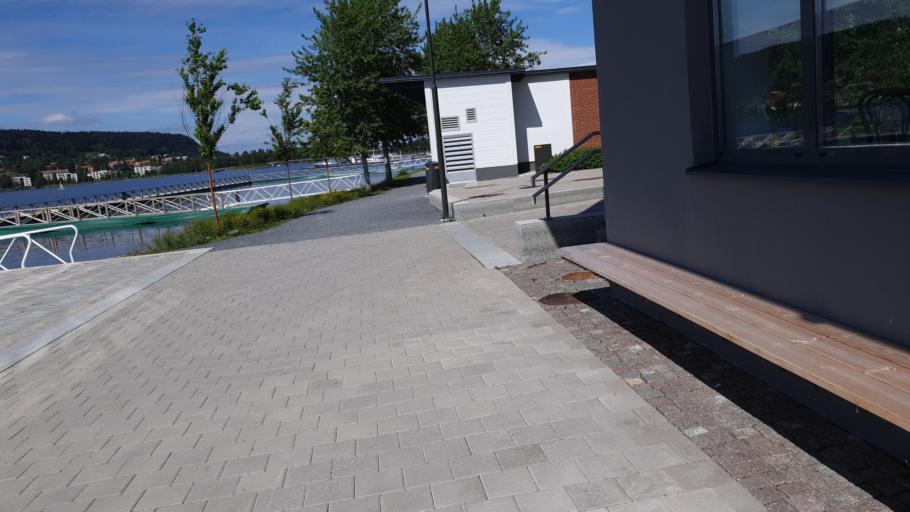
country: SE
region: Jaemtland
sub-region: OEstersunds Kommun
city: Ostersund
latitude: 63.1737
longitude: 14.6308
